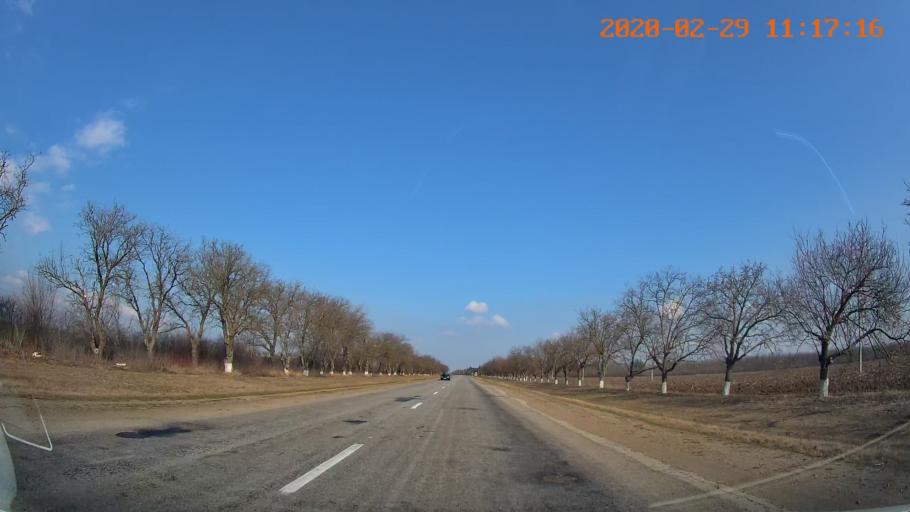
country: MD
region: Telenesti
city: Dubasari
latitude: 47.3199
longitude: 29.1702
